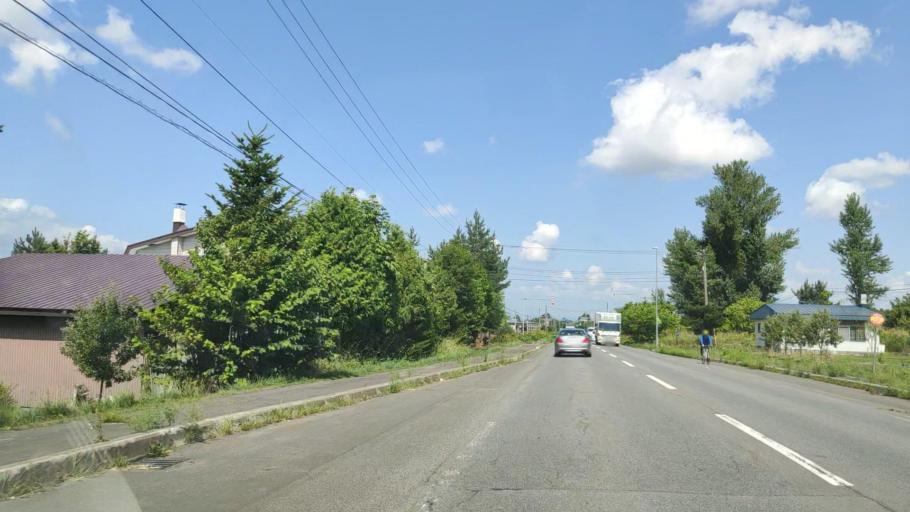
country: JP
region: Hokkaido
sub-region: Asahikawa-shi
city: Asahikawa
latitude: 43.6360
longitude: 142.4558
